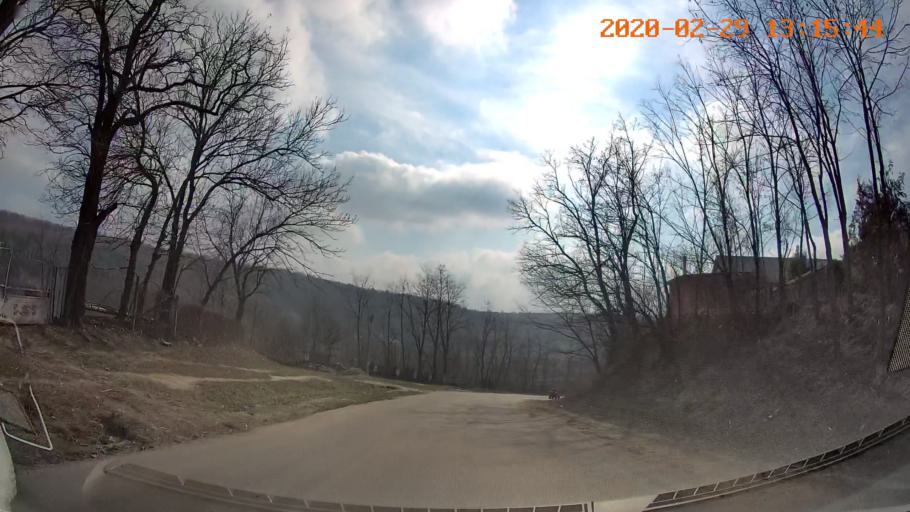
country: MD
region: Telenesti
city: Camenca
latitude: 48.0079
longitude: 28.6682
